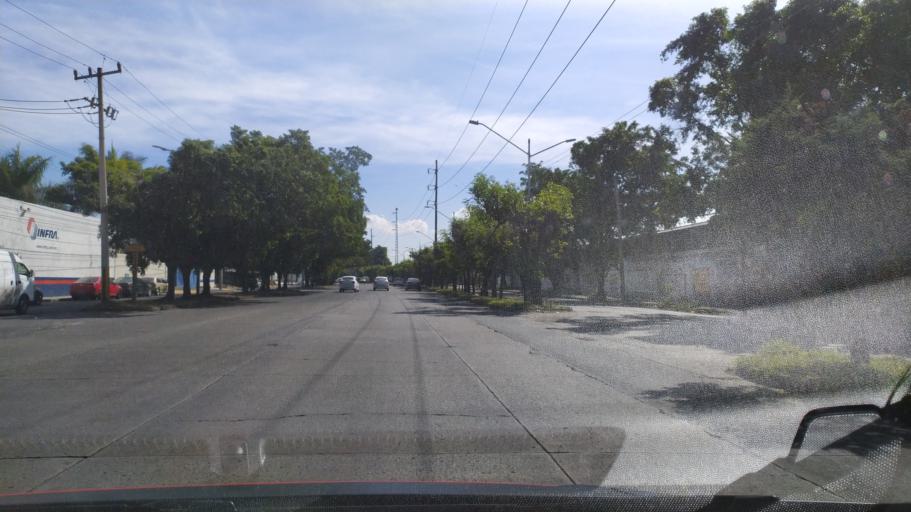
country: MX
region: Jalisco
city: Tlaquepaque
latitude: 20.6431
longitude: -103.3371
